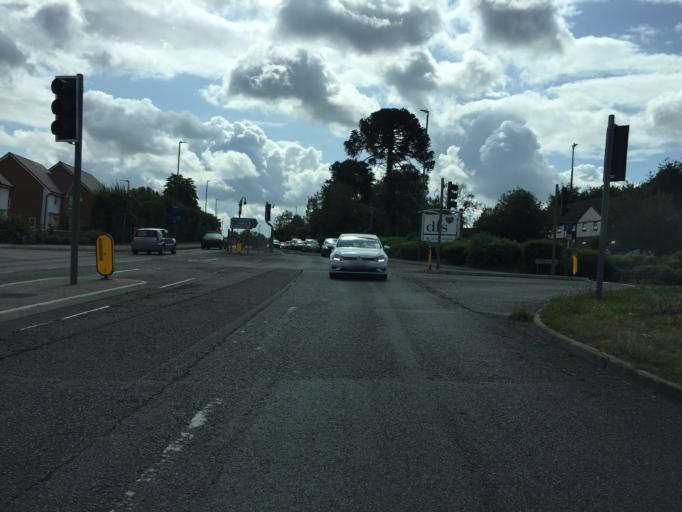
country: GB
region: England
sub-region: Kent
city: Aylesford
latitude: 51.2884
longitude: 0.4899
